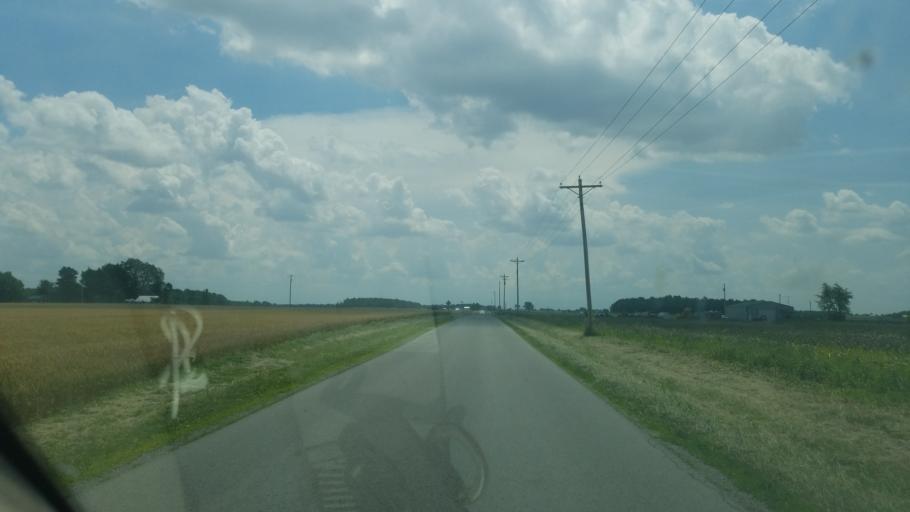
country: US
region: Ohio
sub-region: Hancock County
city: Arlington
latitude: 40.8356
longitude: -83.6000
